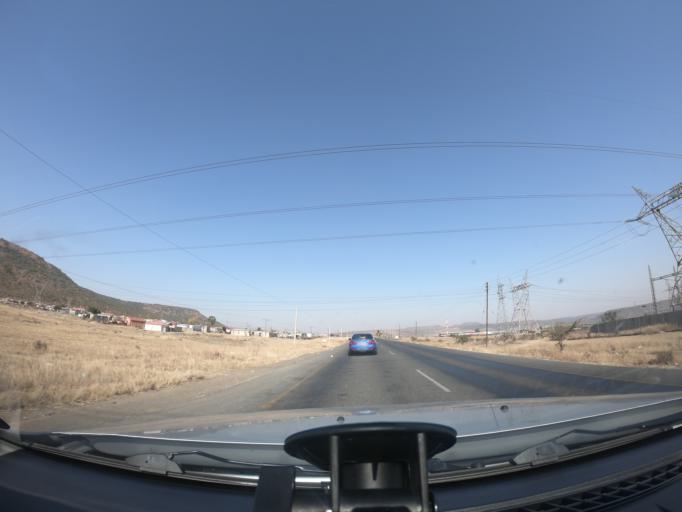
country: ZA
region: KwaZulu-Natal
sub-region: uThukela District Municipality
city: Ladysmith
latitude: -28.5673
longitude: 29.8353
